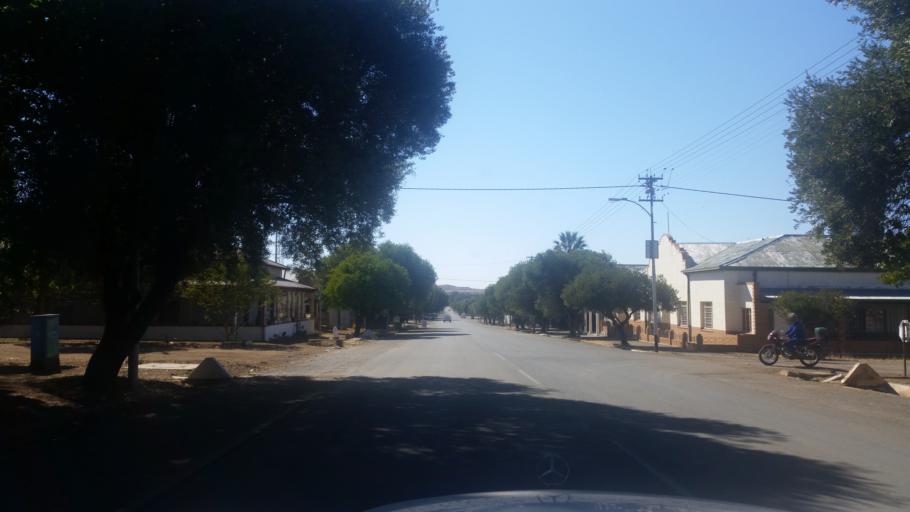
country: ZA
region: Orange Free State
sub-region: Xhariep District Municipality
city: Trompsburg
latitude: -30.4952
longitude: 25.9718
